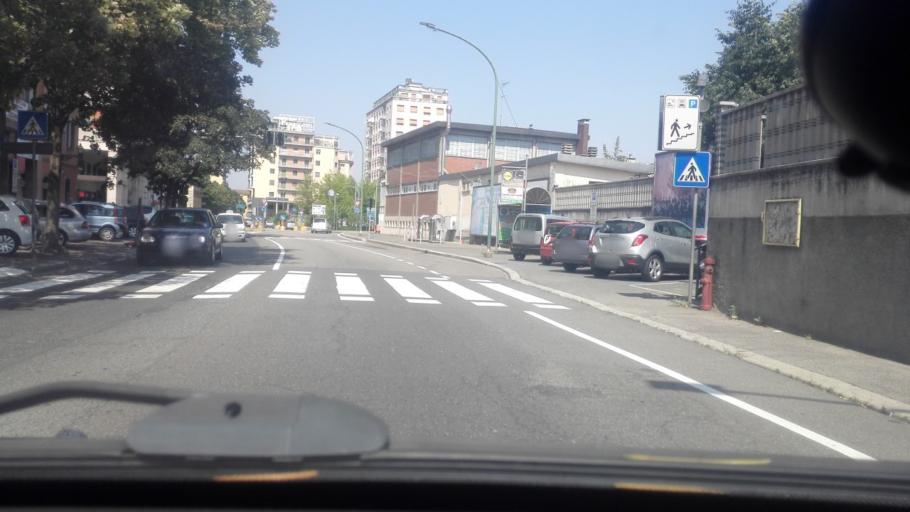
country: IT
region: Piedmont
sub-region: Provincia di Alessandria
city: Novi Ligure
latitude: 44.7616
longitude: 8.7882
